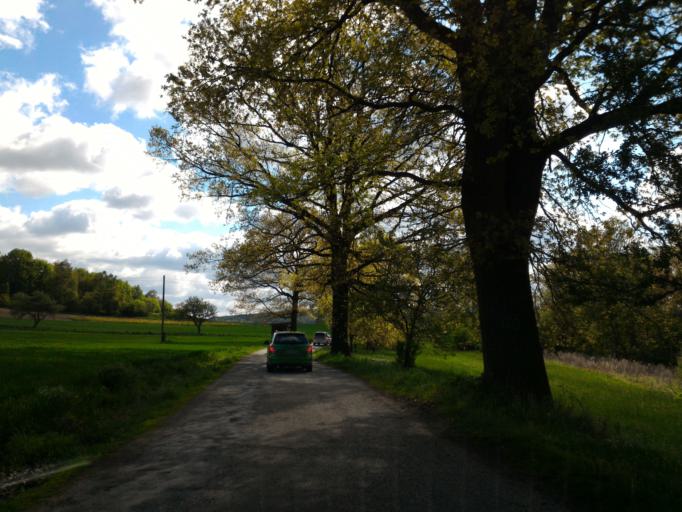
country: CZ
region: Vysocina
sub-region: Okres Havlickuv Brod
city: Svetla nad Sazavou
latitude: 49.6322
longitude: 15.3715
